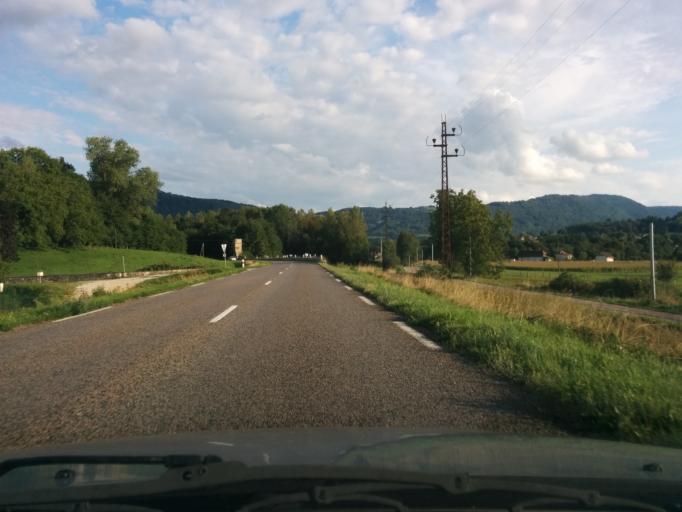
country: FR
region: Rhone-Alpes
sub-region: Departement de la Savoie
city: Domessin
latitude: 45.5146
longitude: 5.7071
